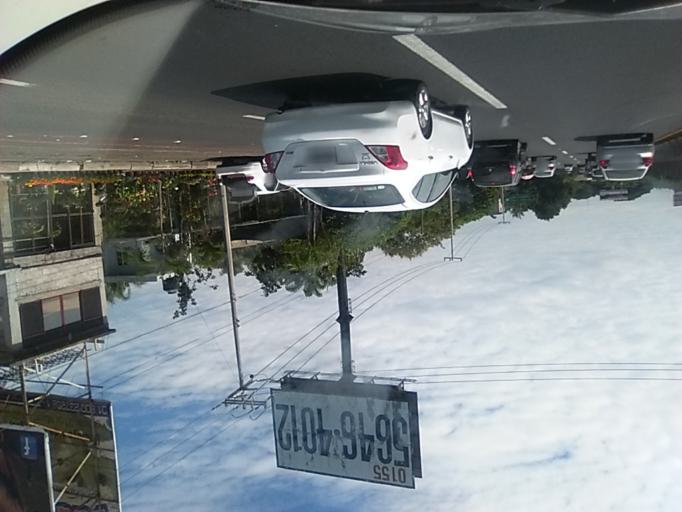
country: MX
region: Morelos
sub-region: Cuernavaca
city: Cuernavaca
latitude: 18.9041
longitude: -99.2153
